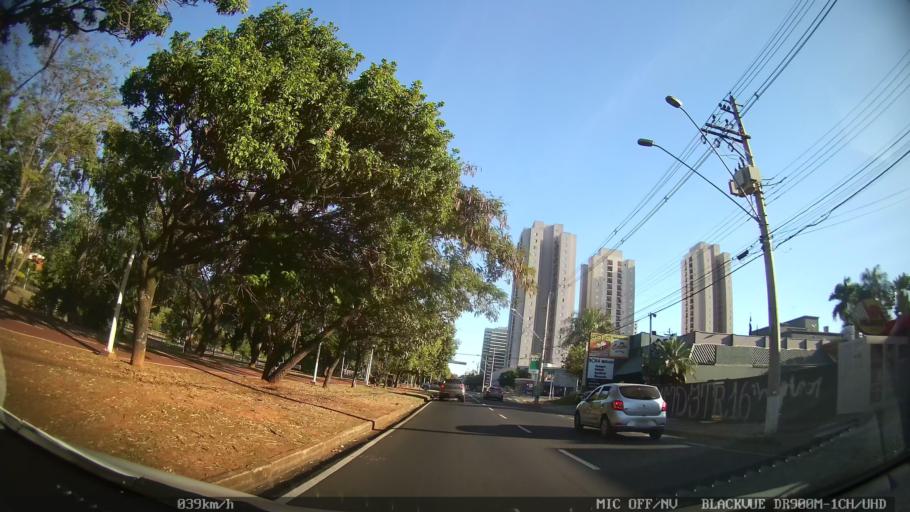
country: BR
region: Sao Paulo
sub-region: Sao Jose Do Rio Preto
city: Sao Jose do Rio Preto
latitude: -20.8359
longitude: -49.4081
